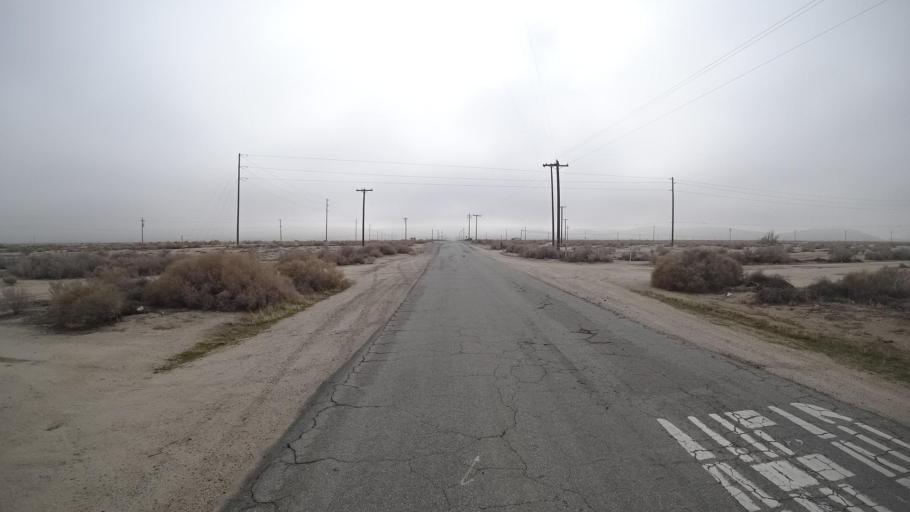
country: US
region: California
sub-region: Kern County
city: Ford City
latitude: 35.1954
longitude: -119.4289
